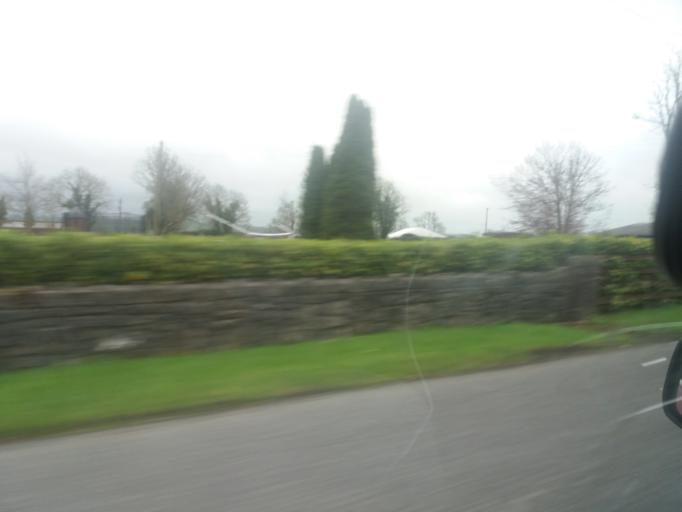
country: IE
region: Munster
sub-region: County Limerick
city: Newcastle West
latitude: 52.4855
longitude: -9.0070
